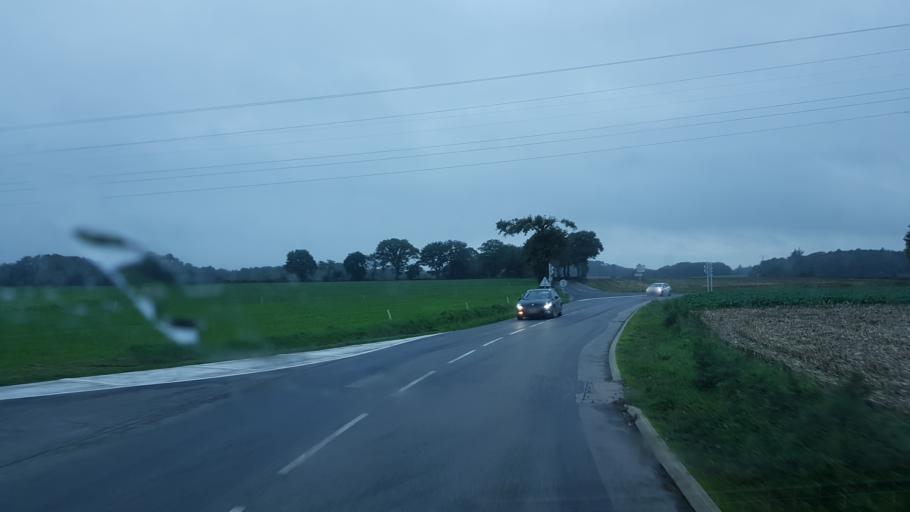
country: FR
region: Brittany
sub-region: Departement du Morbihan
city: Trefflean
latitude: 47.6577
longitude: -2.6259
